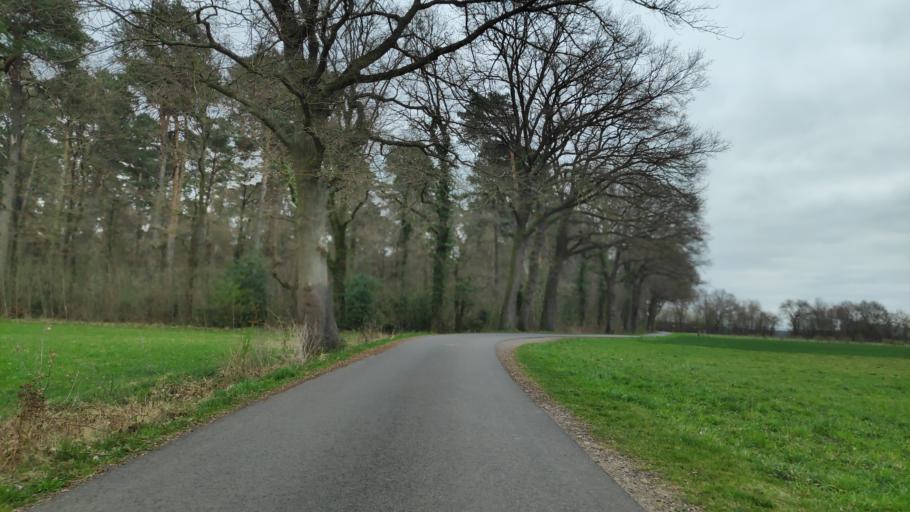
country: DE
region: North Rhine-Westphalia
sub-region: Regierungsbezirk Detmold
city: Petershagen
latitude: 52.3605
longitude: 8.9144
